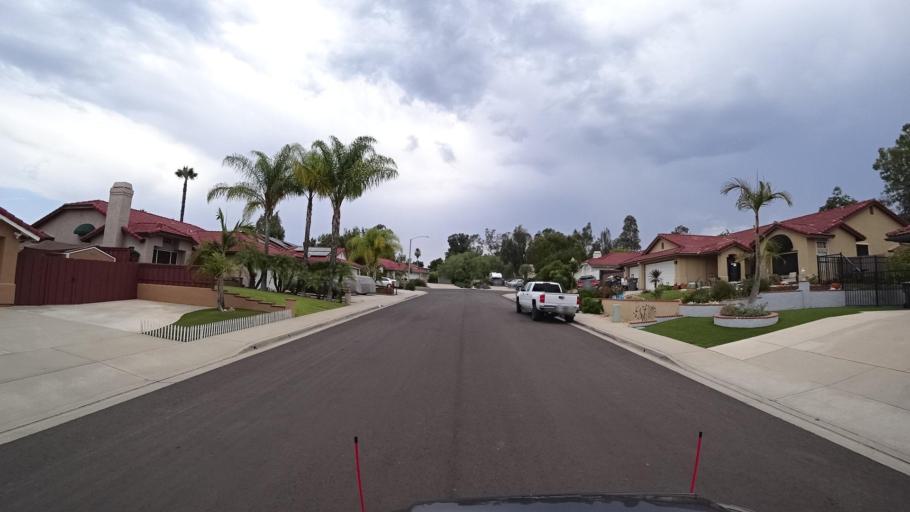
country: US
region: California
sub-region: San Diego County
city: Escondido
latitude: 33.1438
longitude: -117.1133
